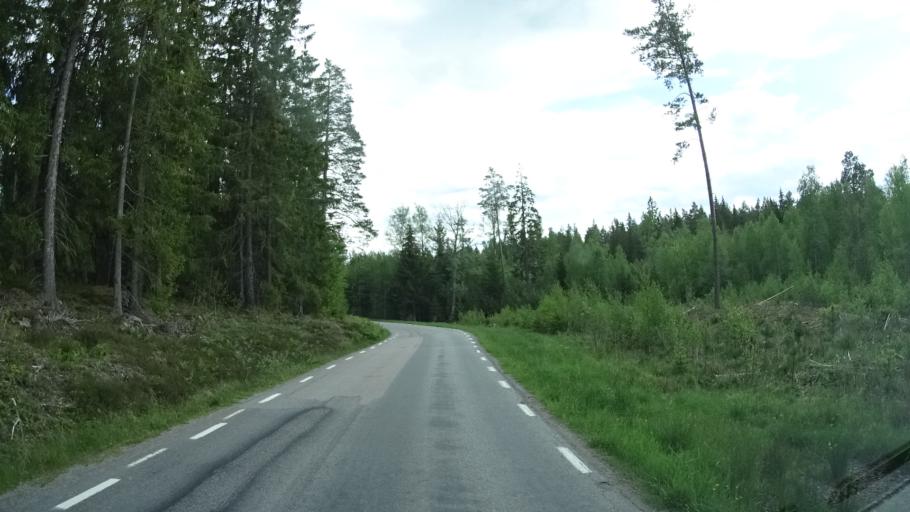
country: SE
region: OEstergoetland
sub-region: Finspangs Kommun
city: Finspang
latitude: 58.6008
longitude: 15.7610
